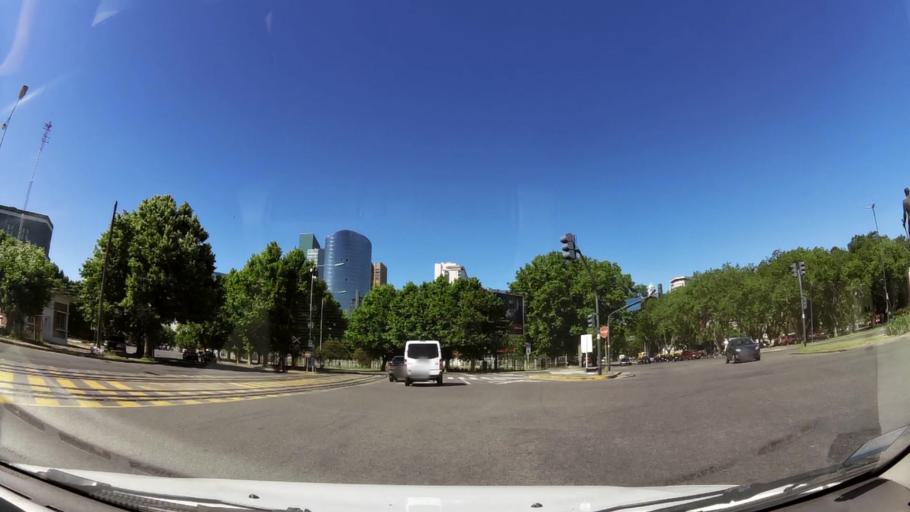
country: AR
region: Buenos Aires F.D.
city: Retiro
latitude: -34.5903
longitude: -58.3705
